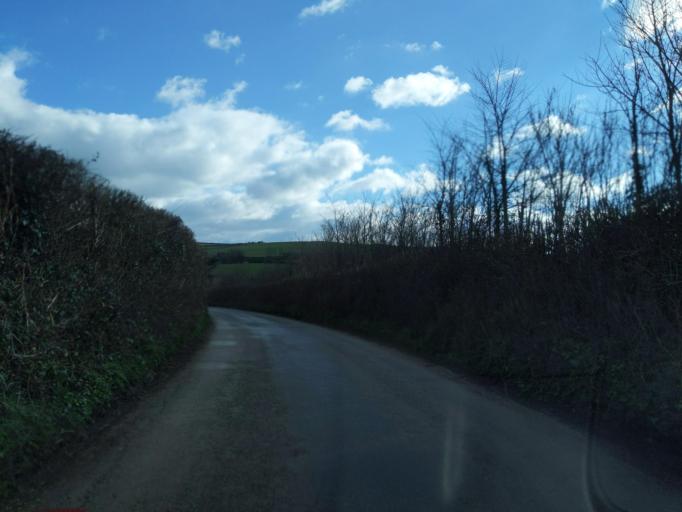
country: GB
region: England
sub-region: Devon
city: Salcombe
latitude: 50.2544
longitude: -3.7046
